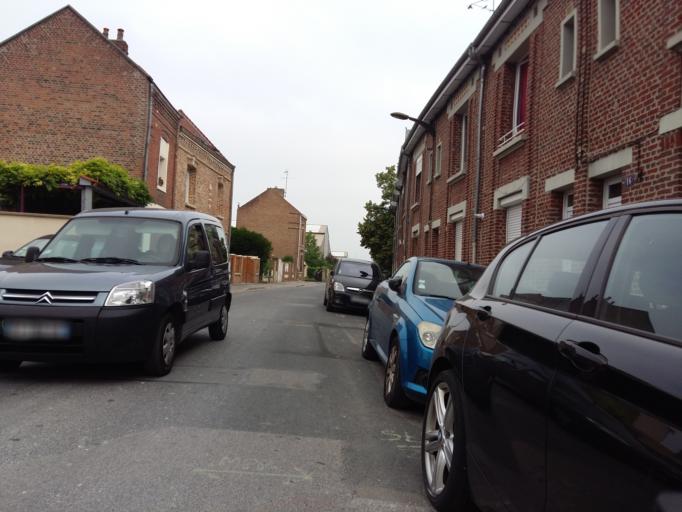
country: FR
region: Picardie
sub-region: Departement de la Somme
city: Amiens
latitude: 49.9087
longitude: 2.2910
